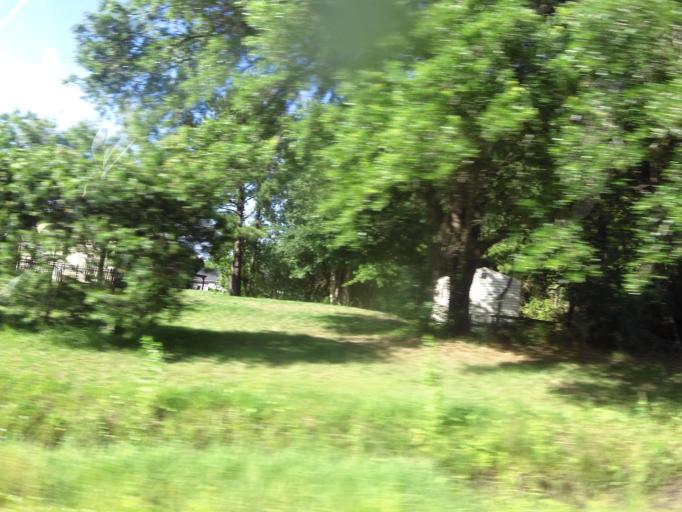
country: US
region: Florida
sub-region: Nassau County
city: Callahan
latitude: 30.5596
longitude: -81.7787
